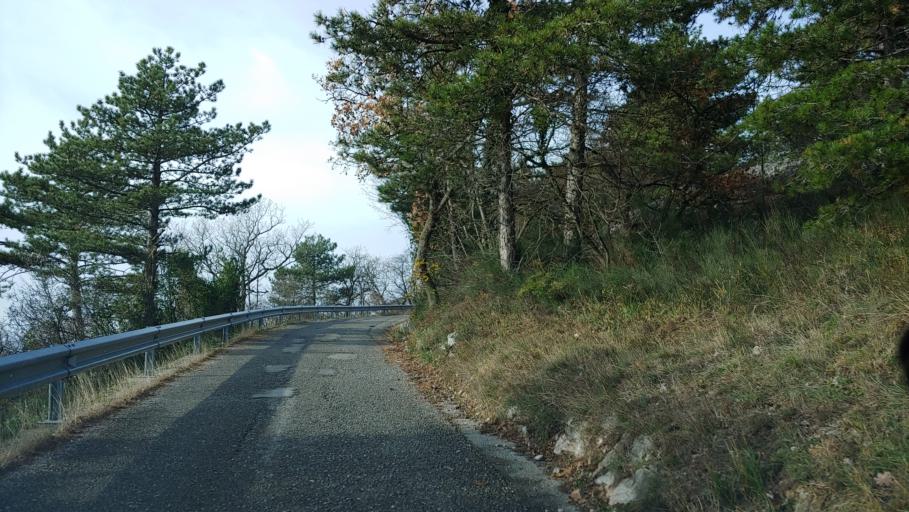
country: IT
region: Friuli Venezia Giulia
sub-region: Provincia di Trieste
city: Duino
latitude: 45.8191
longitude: 13.6201
